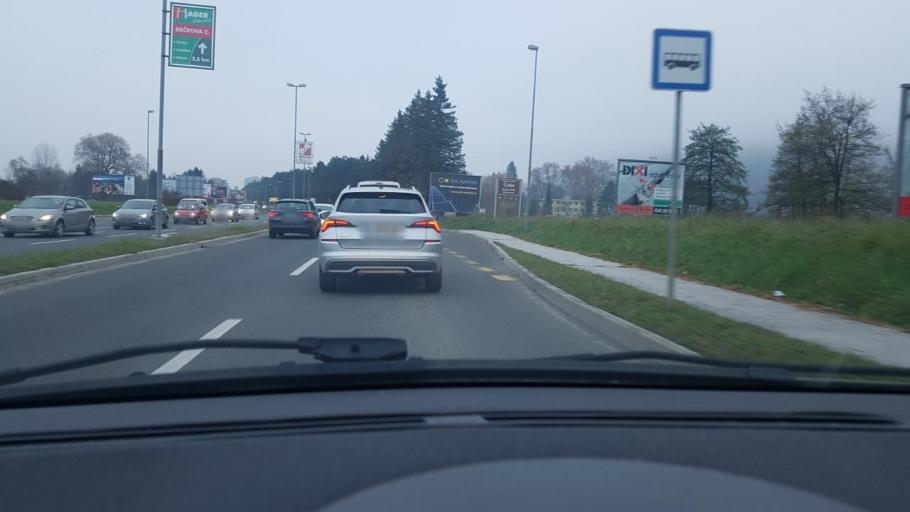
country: SI
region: Celje
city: Celje
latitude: 46.2383
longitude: 15.2297
